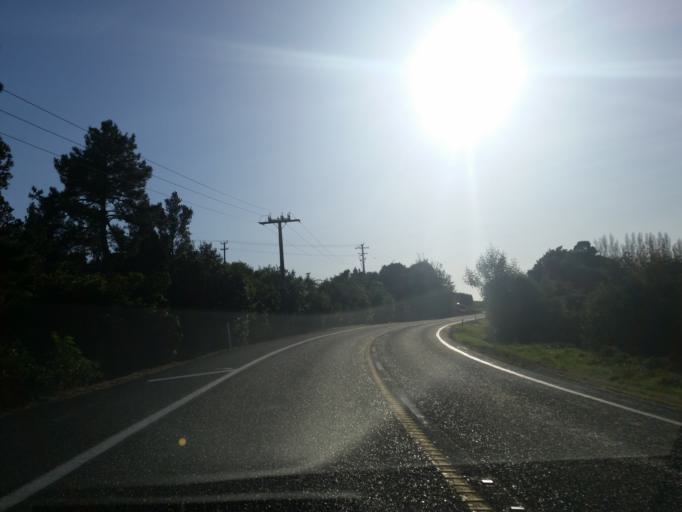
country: NZ
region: Bay of Plenty
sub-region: Western Bay of Plenty District
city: Katikati
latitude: -37.5276
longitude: 175.9144
